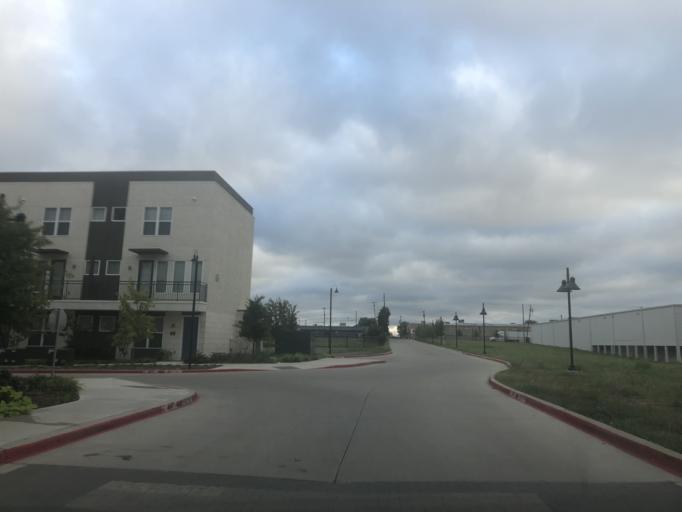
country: US
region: Texas
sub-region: Dallas County
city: University Park
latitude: 32.8280
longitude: -96.8475
